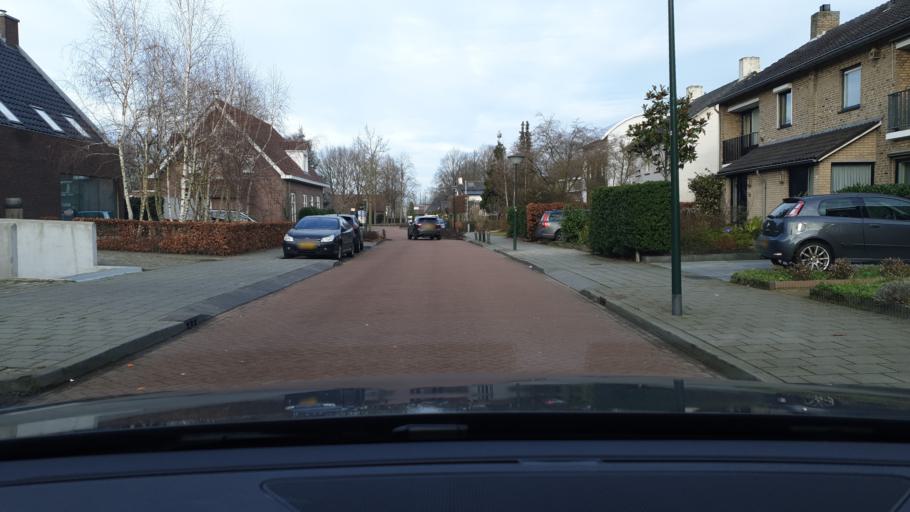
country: NL
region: North Brabant
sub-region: Gemeente Geldrop-Mierlo
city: Geldrop
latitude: 51.4275
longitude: 5.5454
